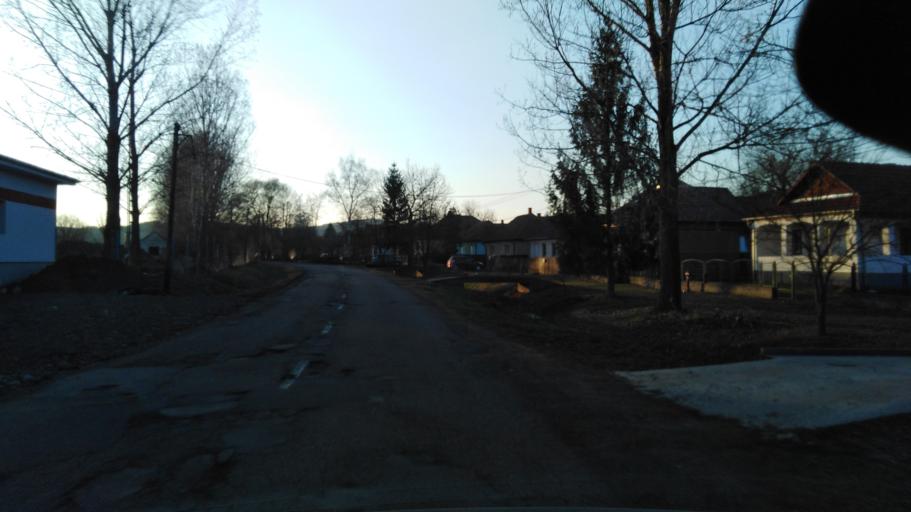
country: HU
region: Nograd
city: Kazar
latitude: 48.0500
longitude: 19.8494
